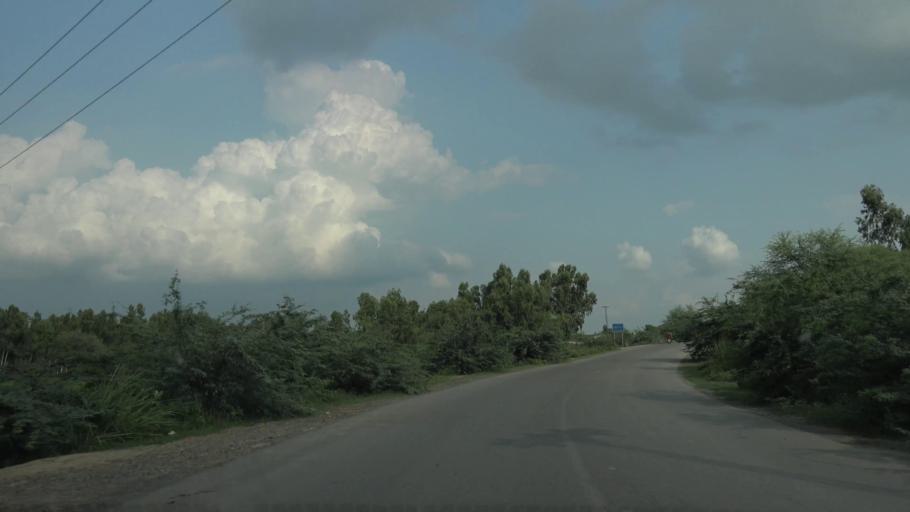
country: PK
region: Punjab
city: Nankana Sahib
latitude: 31.4941
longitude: 73.6030
